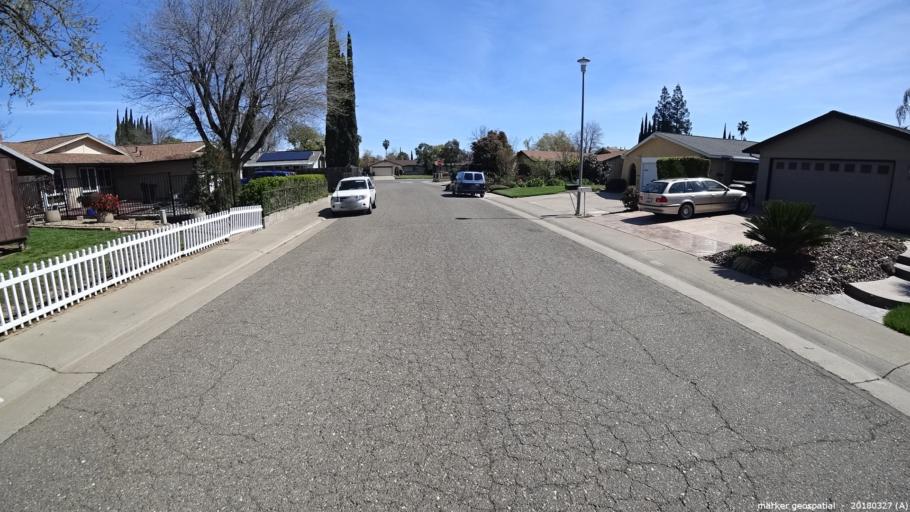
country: US
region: California
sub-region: Sacramento County
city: La Riviera
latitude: 38.5565
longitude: -121.3548
